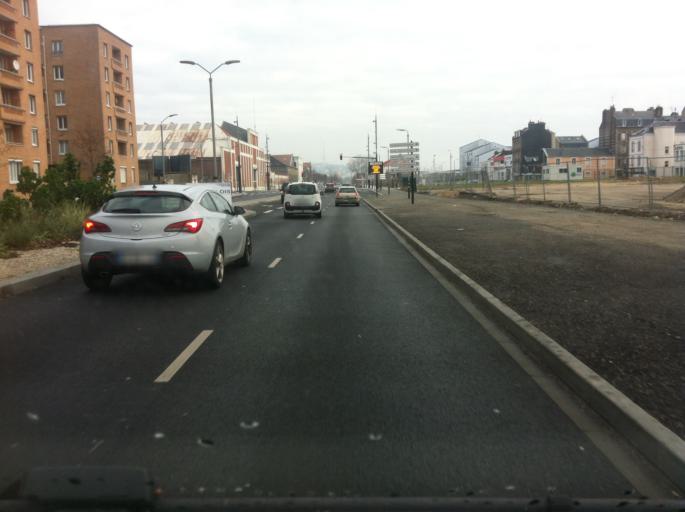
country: FR
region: Haute-Normandie
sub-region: Departement de la Seine-Maritime
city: Le Havre
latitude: 49.4936
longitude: 0.1367
